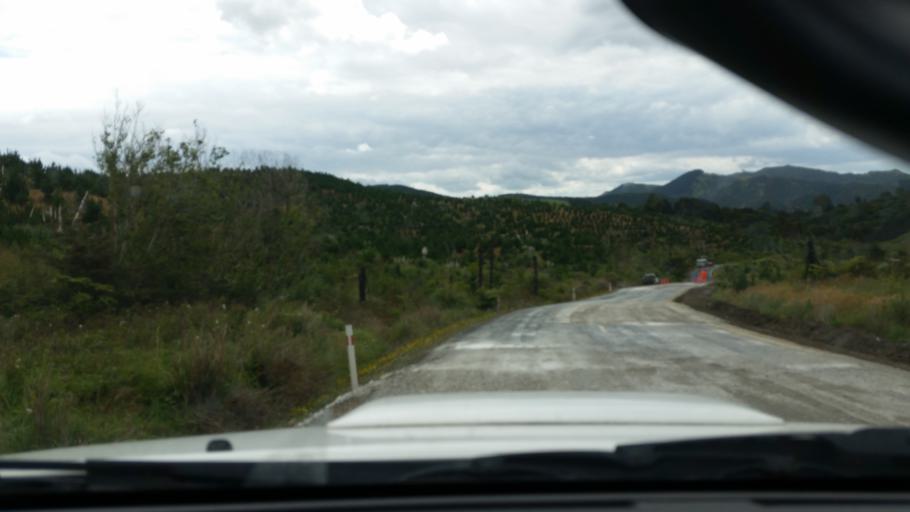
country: NZ
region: Northland
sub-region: Kaipara District
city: Dargaville
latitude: -35.7236
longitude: 173.8592
